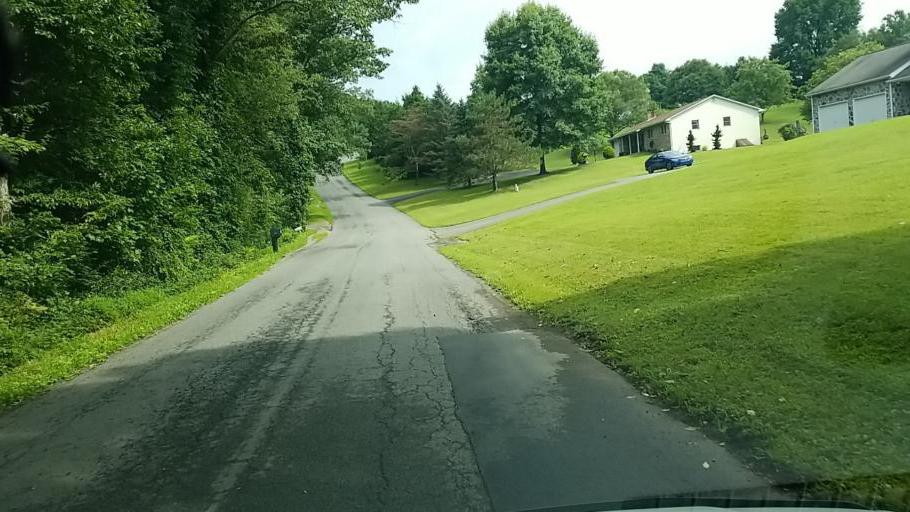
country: US
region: Pennsylvania
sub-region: Dauphin County
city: Matamoras
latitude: 40.4913
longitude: -76.9224
